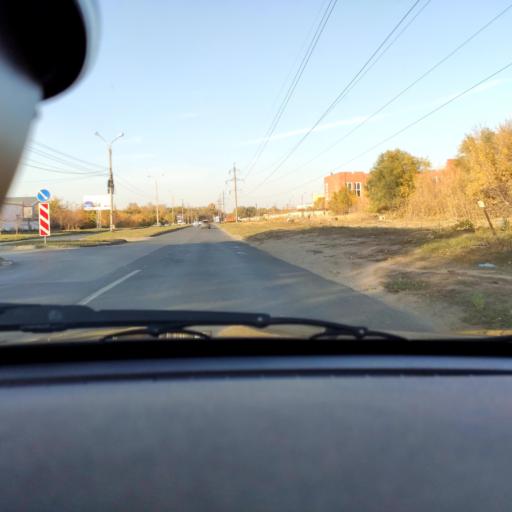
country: RU
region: Samara
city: Tol'yatti
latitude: 53.5544
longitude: 49.3189
